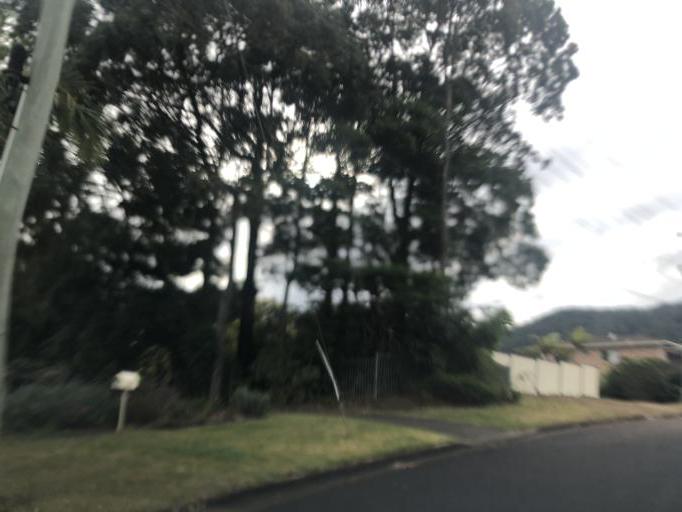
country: AU
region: New South Wales
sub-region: Coffs Harbour
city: Coffs Harbour
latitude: -30.2784
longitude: 153.1108
